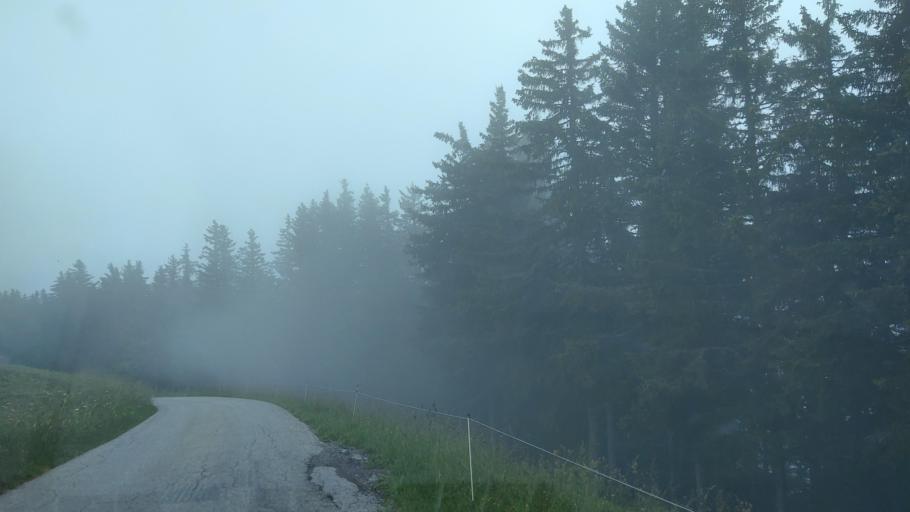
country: FR
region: Rhone-Alpes
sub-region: Departement de la Savoie
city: Beaufort
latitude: 45.7471
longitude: 6.5248
